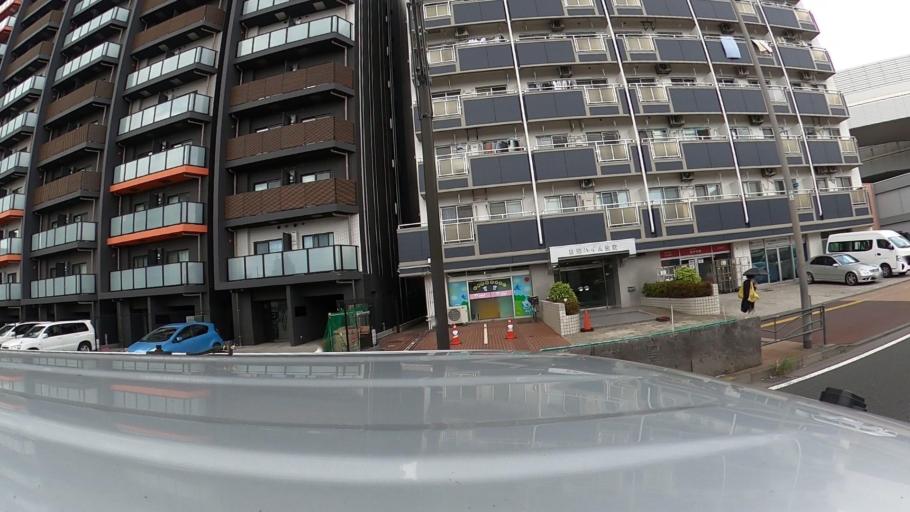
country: JP
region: Kanagawa
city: Yokohama
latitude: 35.4906
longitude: 139.6618
